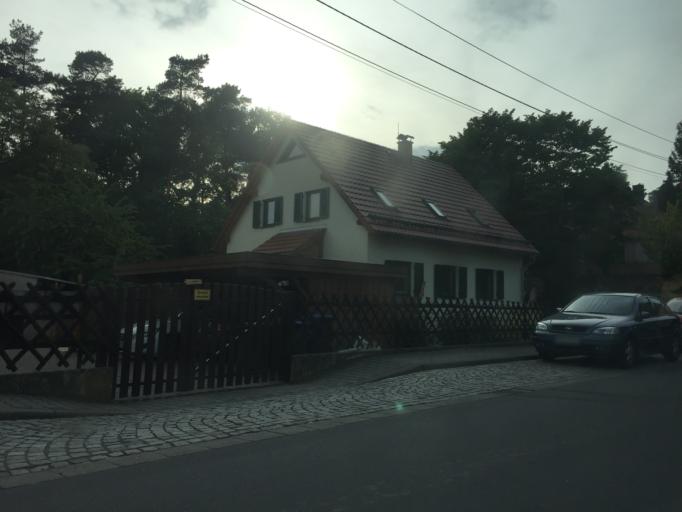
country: DE
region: Saxony
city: Heidenau
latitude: 50.9951
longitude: 13.9074
